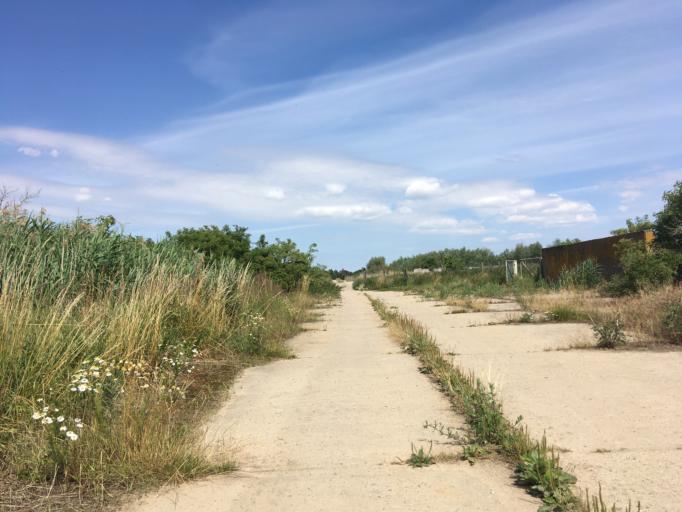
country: DE
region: Brandenburg
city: Casekow
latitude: 53.2232
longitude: 14.1390
